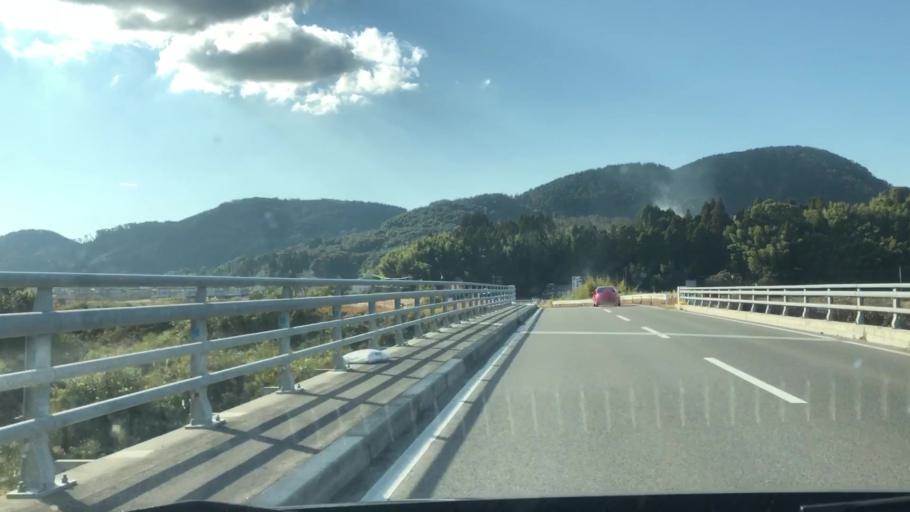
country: JP
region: Kagoshima
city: Satsumasendai
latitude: 31.8652
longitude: 130.3268
